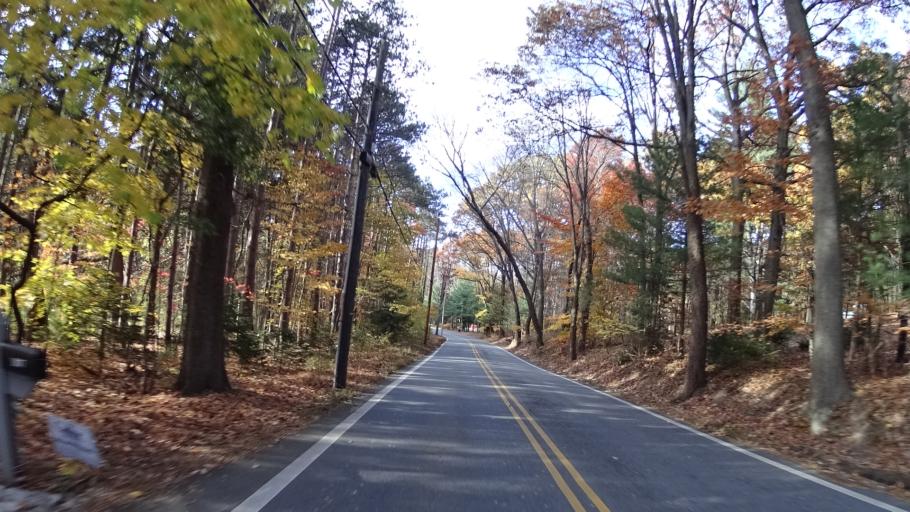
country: US
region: New Jersey
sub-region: Morris County
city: Morristown
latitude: 40.7521
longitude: -74.5150
